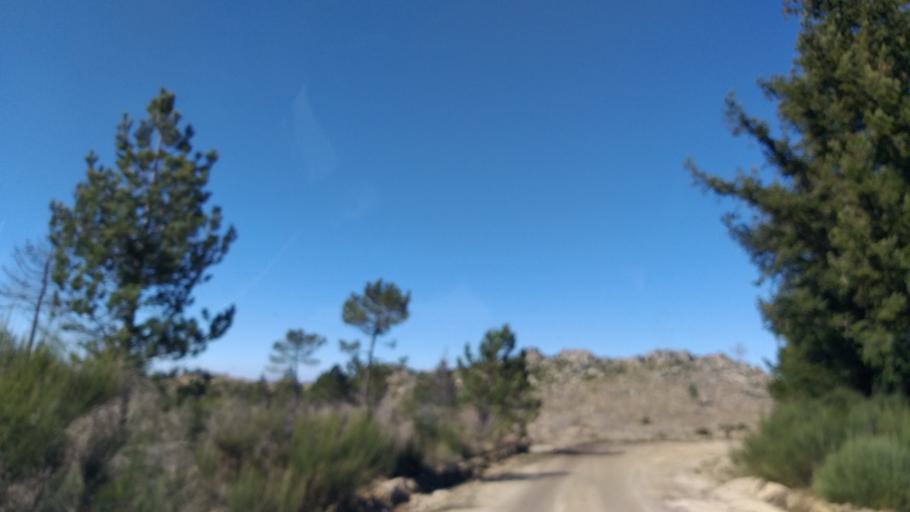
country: PT
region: Guarda
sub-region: Manteigas
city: Manteigas
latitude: 40.4990
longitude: -7.4896
